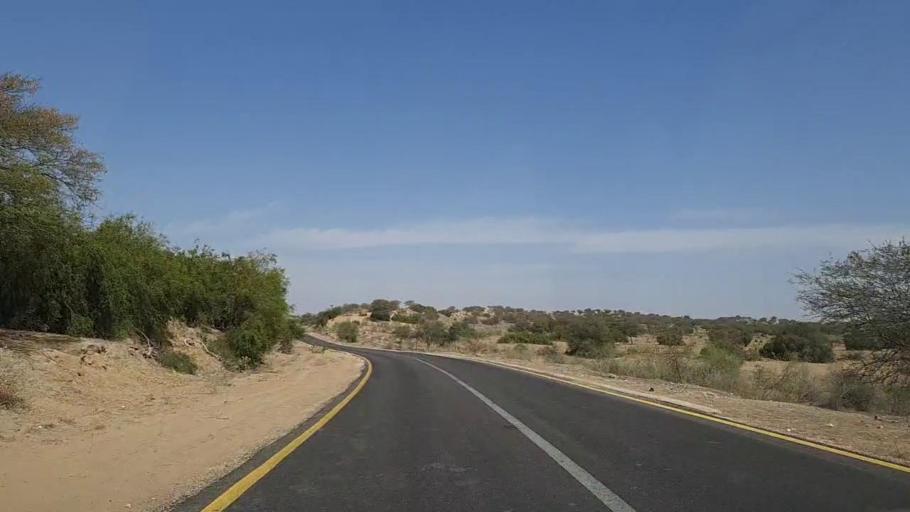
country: PK
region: Sindh
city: Mithi
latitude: 24.9034
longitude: 69.8874
